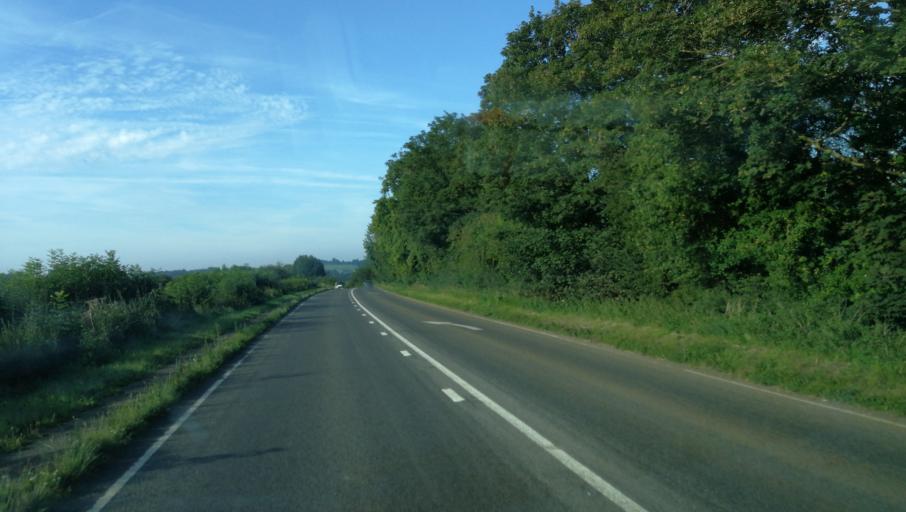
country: GB
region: England
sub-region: Oxfordshire
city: Adderbury
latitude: 52.0048
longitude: -1.3182
